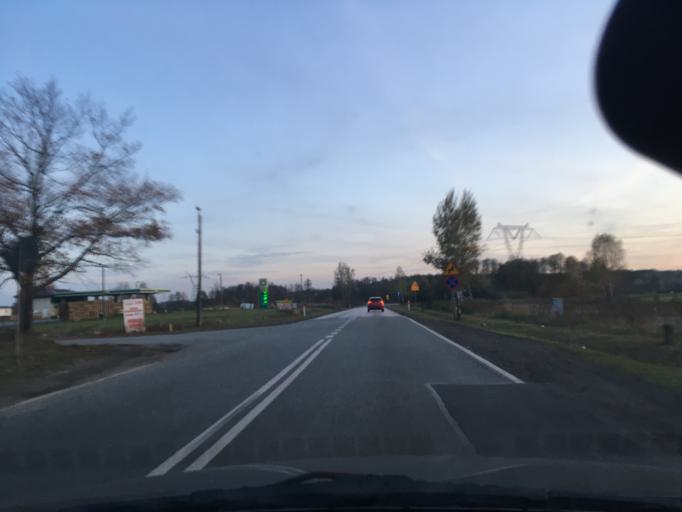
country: PL
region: Masovian Voivodeship
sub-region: Powiat sochaczewski
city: Mlodzieszyn
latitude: 52.3355
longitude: 20.2156
